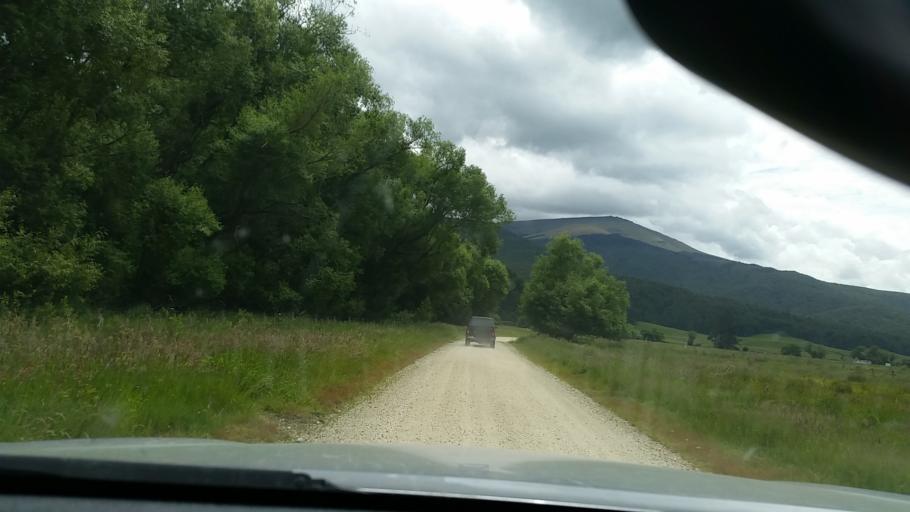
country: NZ
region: Otago
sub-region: Queenstown-Lakes District
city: Kingston
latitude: -45.5892
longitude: 168.9942
